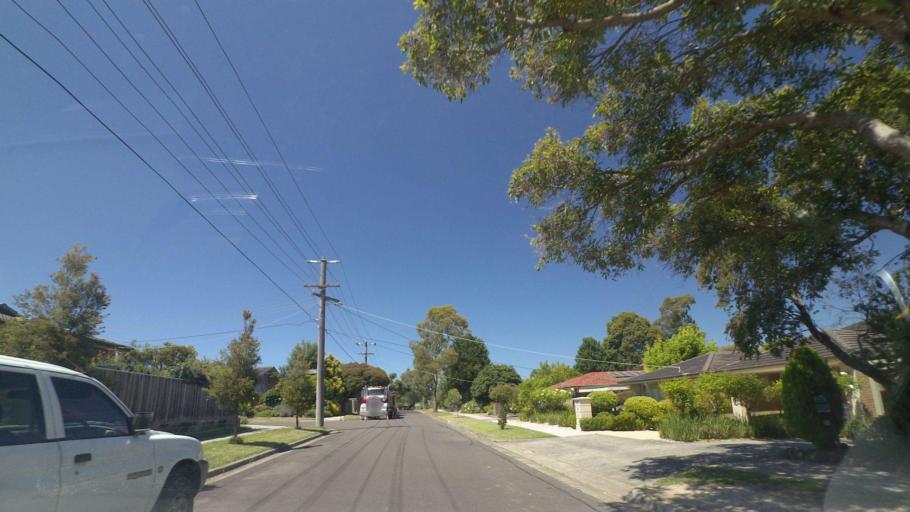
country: AU
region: Victoria
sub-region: Maroondah
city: Warranwood
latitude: -37.7855
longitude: 145.2380
